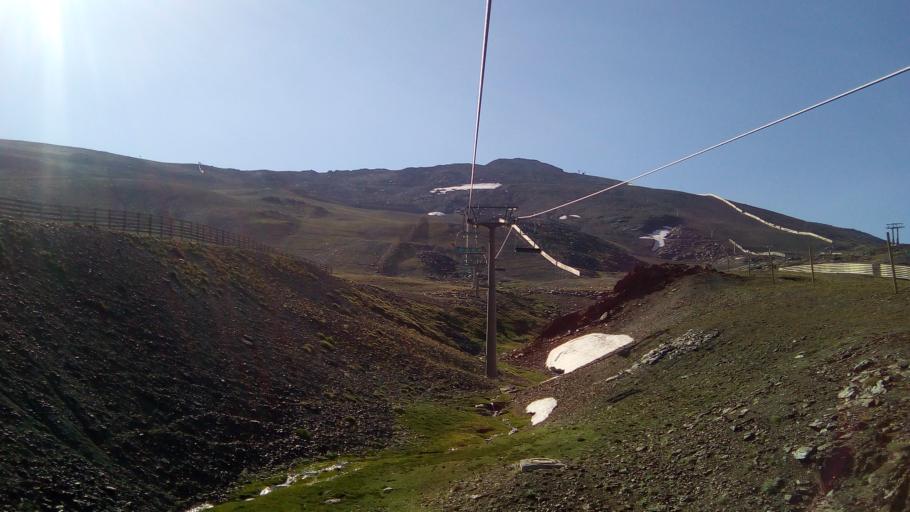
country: ES
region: Andalusia
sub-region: Provincia de Granada
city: Capileira
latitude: 37.0668
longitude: -3.3806
